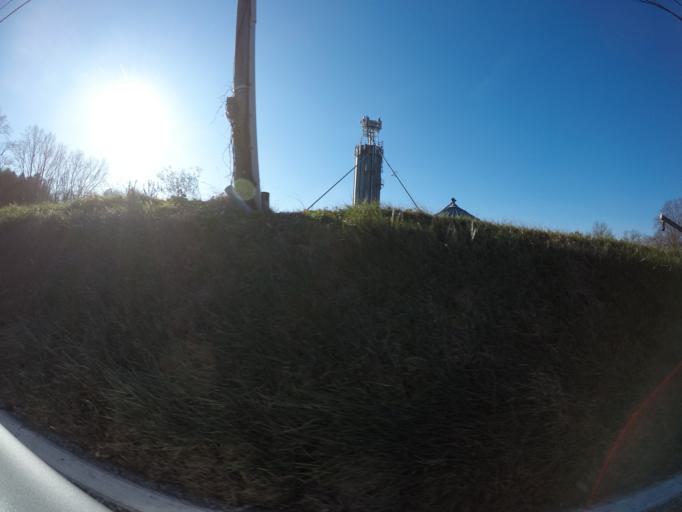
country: US
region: Maryland
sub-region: Harford County
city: South Bel Air
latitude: 39.5901
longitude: -76.2589
